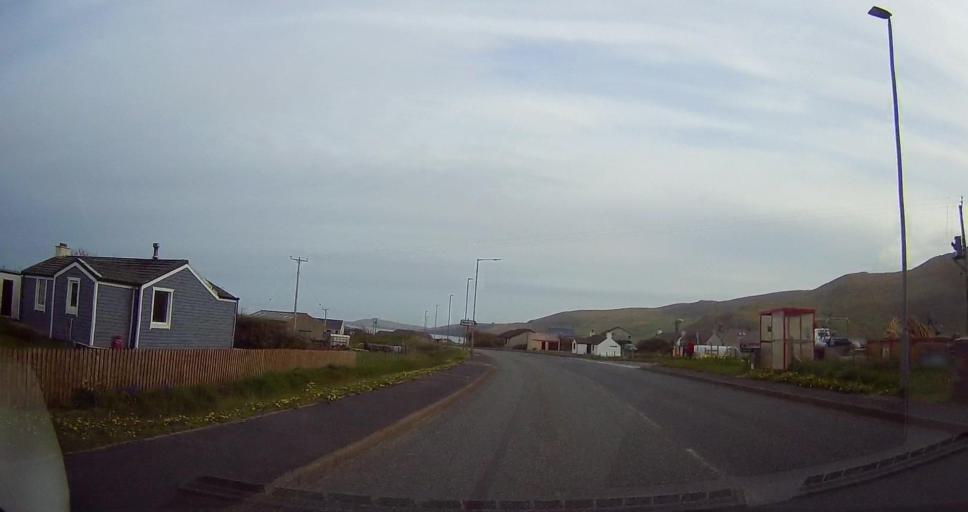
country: GB
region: Scotland
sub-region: Shetland Islands
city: Sandwick
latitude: 60.0411
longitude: -1.2297
